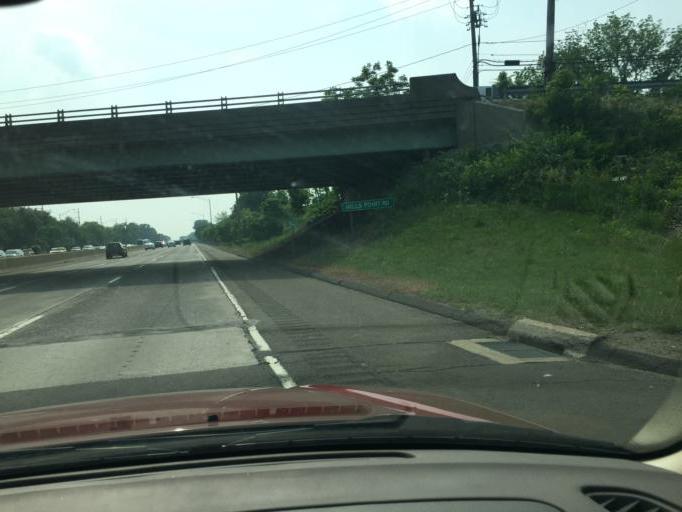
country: US
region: Connecticut
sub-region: Fairfield County
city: Westport
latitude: 41.1232
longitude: -73.3456
